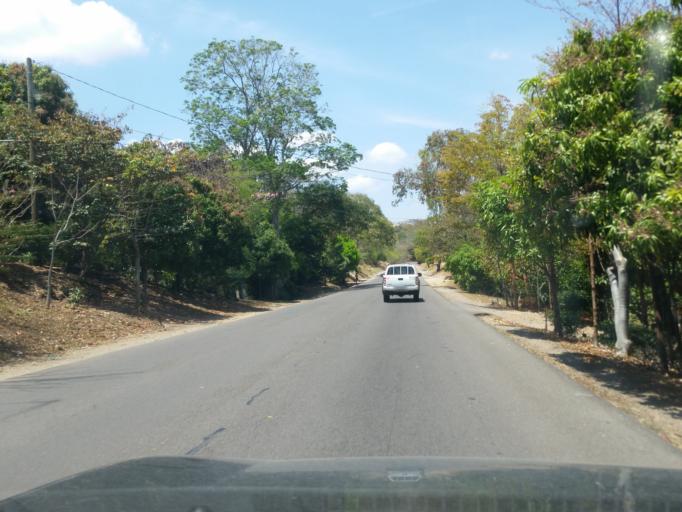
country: NI
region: Esteli
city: Esteli
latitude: 12.9953
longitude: -86.2946
